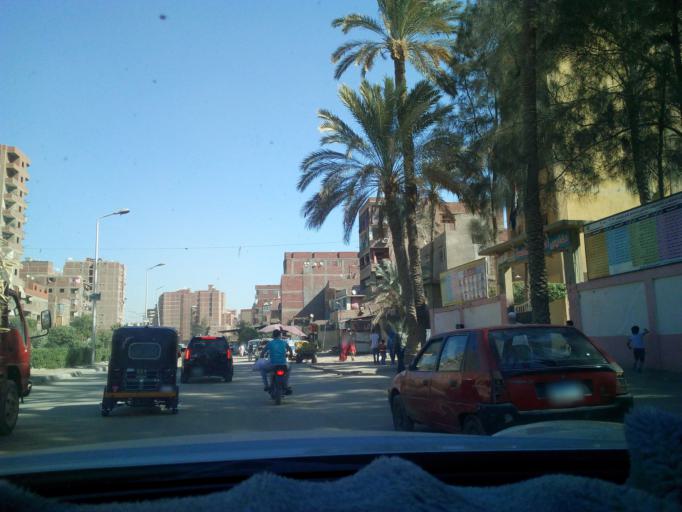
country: EG
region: Muhafazat al Qalyubiyah
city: Al Khankah
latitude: 30.1412
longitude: 31.3493
